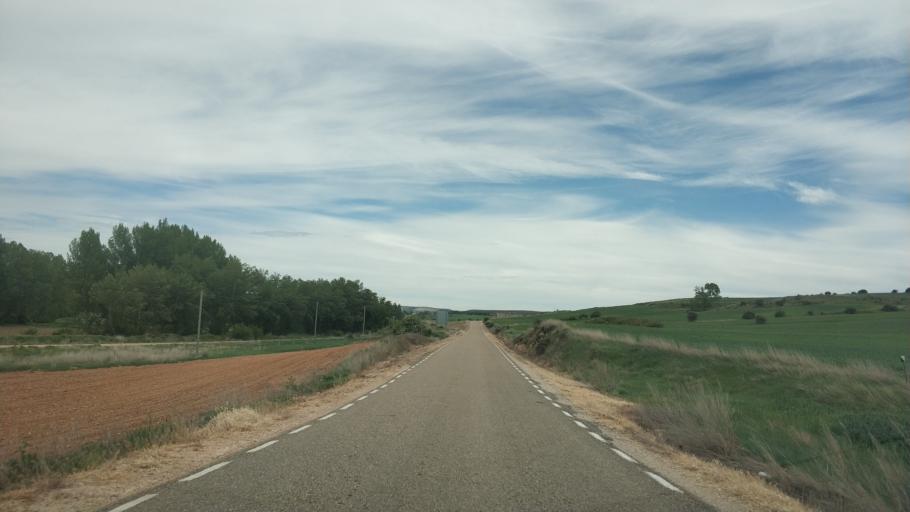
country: ES
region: Castille and Leon
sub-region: Provincia de Soria
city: Berlanga de Duero
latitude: 41.4527
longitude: -2.8452
